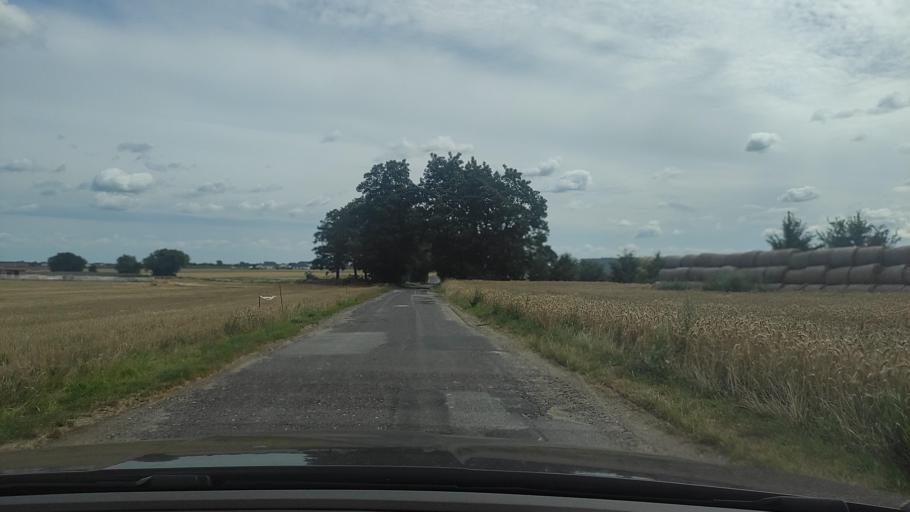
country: PL
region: Greater Poland Voivodeship
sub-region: Powiat poznanski
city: Kostrzyn
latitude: 52.4076
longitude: 17.1940
